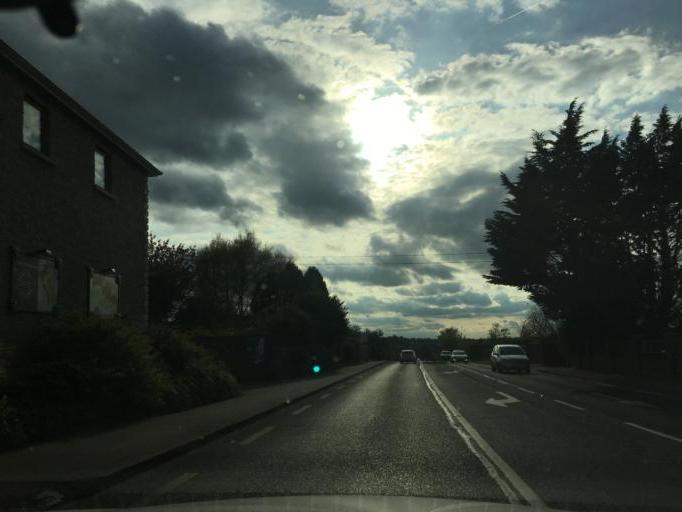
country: IE
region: Leinster
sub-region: Loch Garman
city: Loch Garman
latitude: 52.3409
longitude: -6.5023
